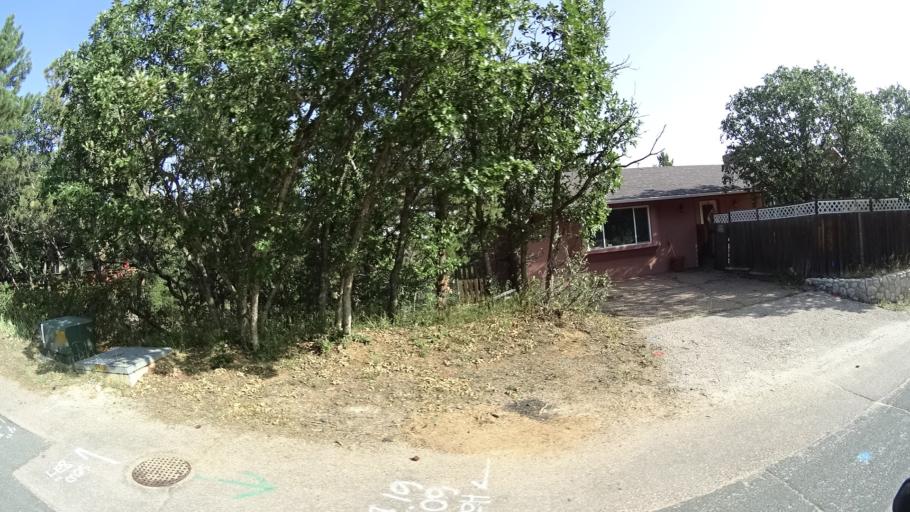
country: US
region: Colorado
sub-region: El Paso County
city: Colorado Springs
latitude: 38.8111
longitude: -104.8715
